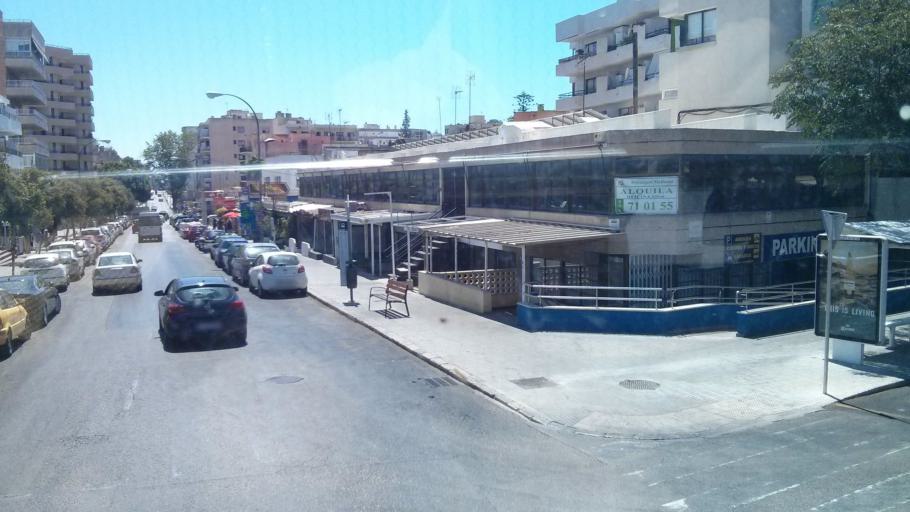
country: ES
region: Balearic Islands
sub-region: Illes Balears
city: Palma
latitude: 39.5671
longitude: 2.6271
